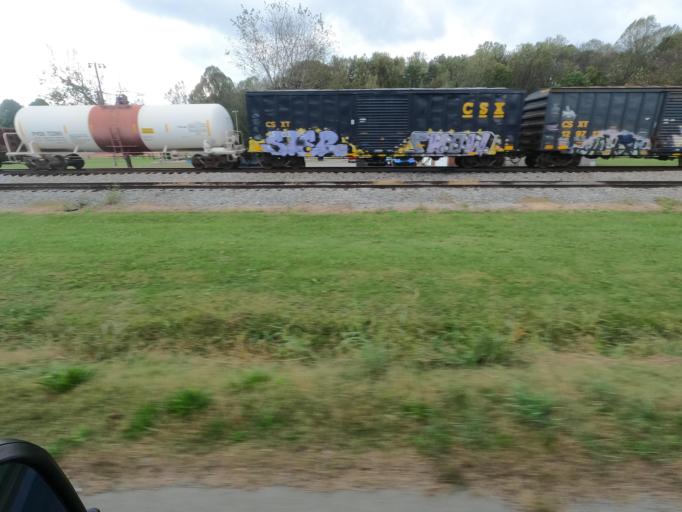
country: US
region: Tennessee
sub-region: Cheatham County
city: Pegram
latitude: 36.1020
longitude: -87.0539
